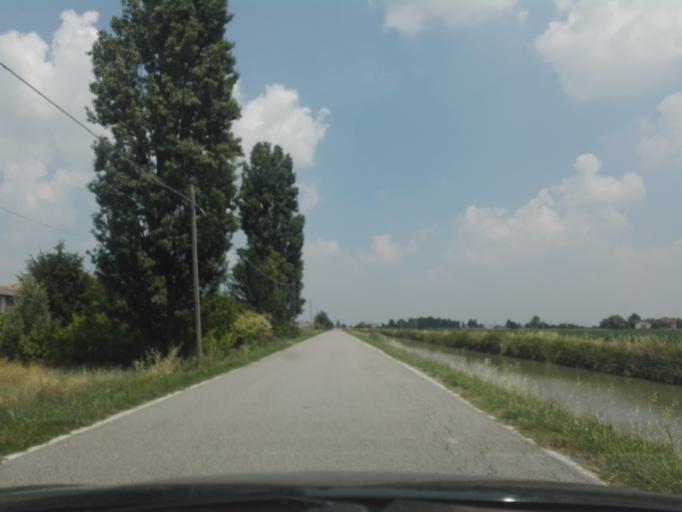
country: IT
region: Veneto
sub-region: Provincia di Rovigo
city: Gavello
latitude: 45.0082
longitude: 11.9085
